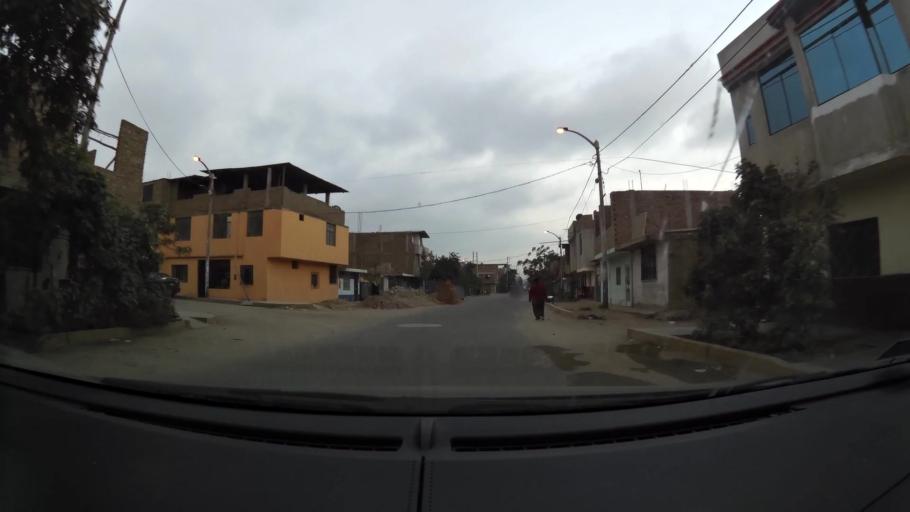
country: PE
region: La Libertad
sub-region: Provincia de Trujillo
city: El Porvenir
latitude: -8.0806
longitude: -79.0171
